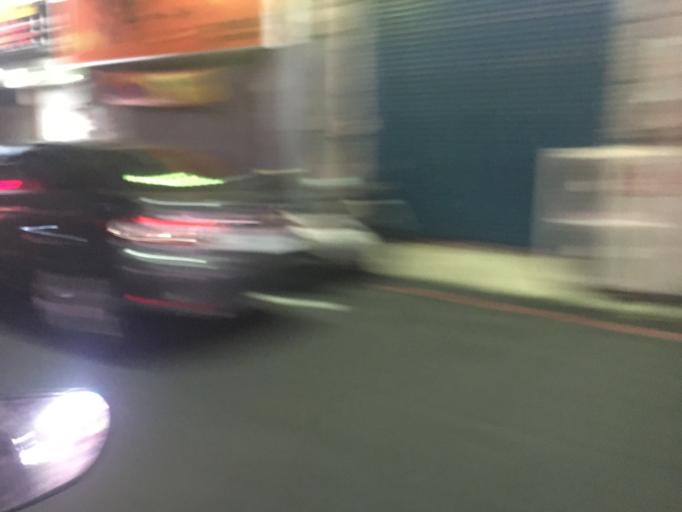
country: TW
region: Taiwan
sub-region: Hsinchu
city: Hsinchu
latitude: 24.8126
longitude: 120.9751
